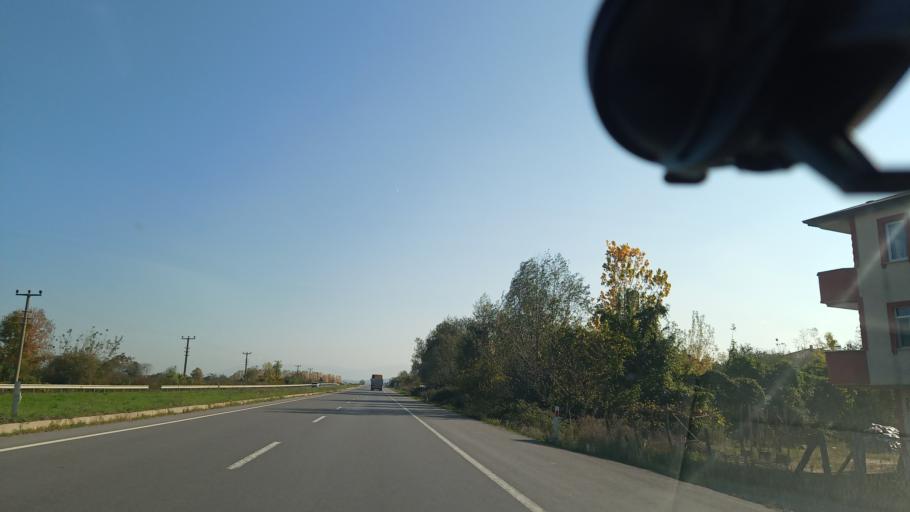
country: TR
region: Sakarya
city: Karasu
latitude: 41.0749
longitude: 30.7843
